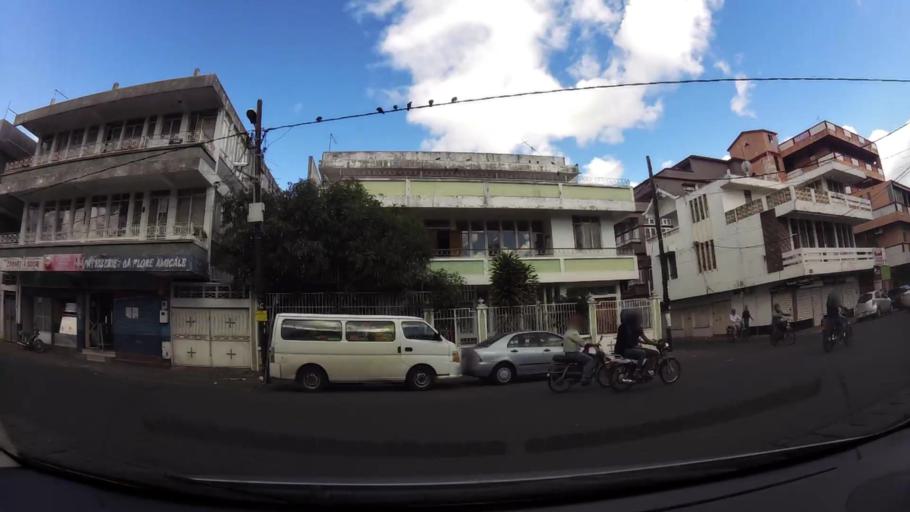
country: MU
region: Port Louis
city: Port Louis
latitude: -20.1606
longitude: 57.5129
